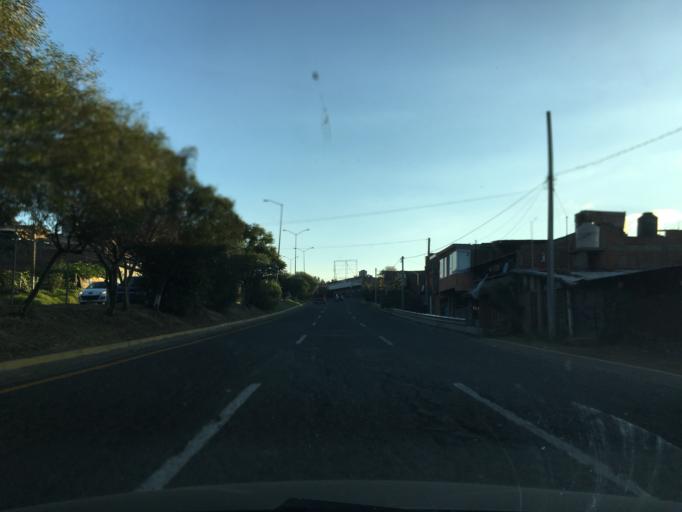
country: MX
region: Michoacan
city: Patzcuaro
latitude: 19.5272
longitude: -101.6146
